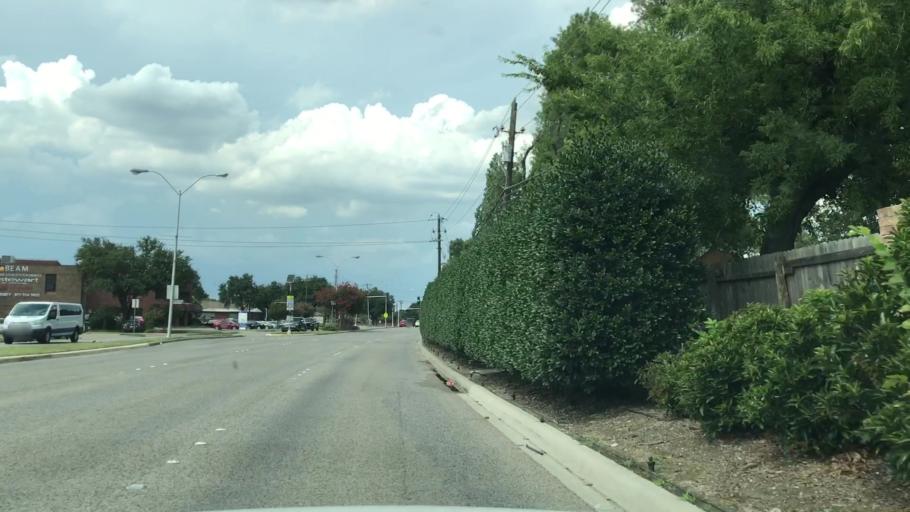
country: US
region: Texas
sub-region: Dallas County
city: Carrollton
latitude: 32.9446
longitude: -96.8727
